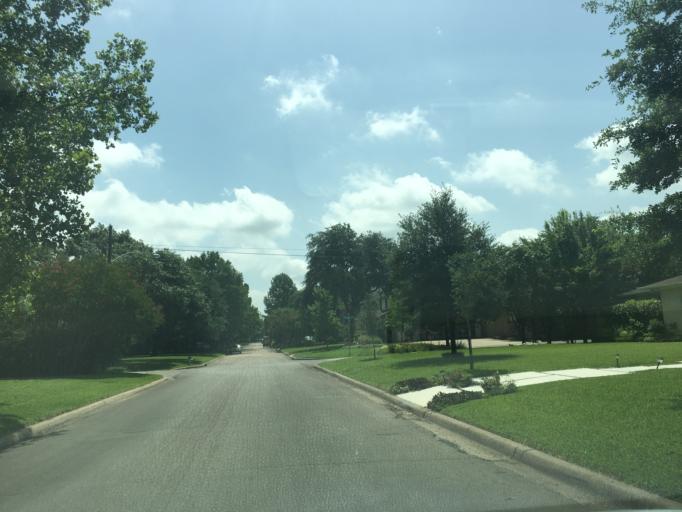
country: US
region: Texas
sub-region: Dallas County
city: University Park
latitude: 32.8792
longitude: -96.8003
